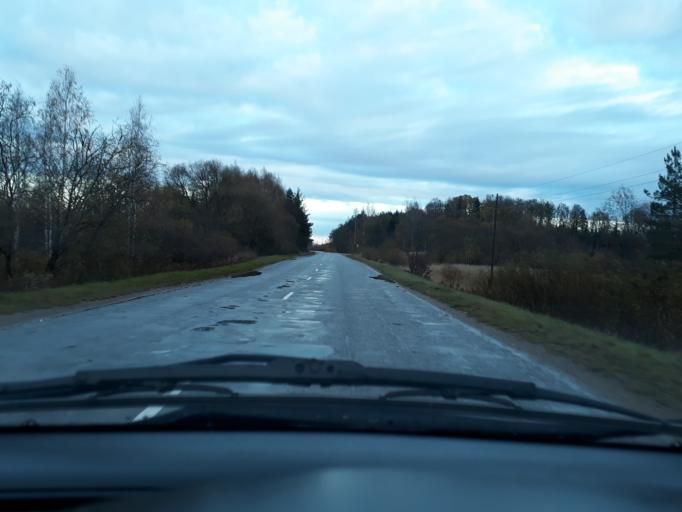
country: LV
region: Dobeles Rajons
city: Dobele
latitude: 56.6127
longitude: 23.2444
